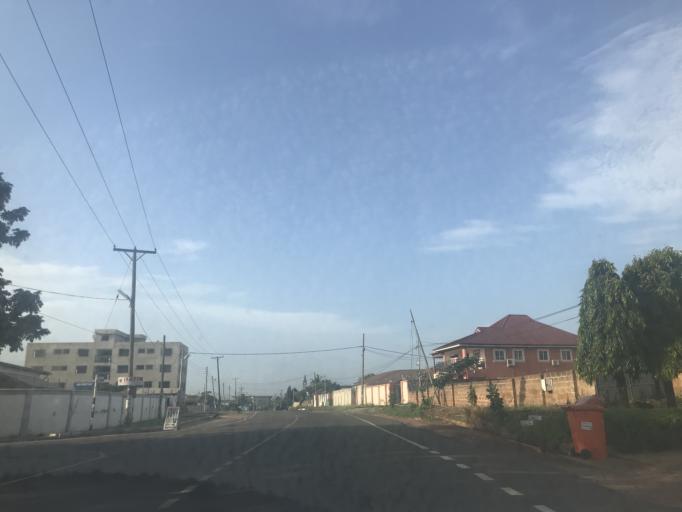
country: GH
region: Greater Accra
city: Medina Estates
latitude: 5.6693
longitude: -0.1776
